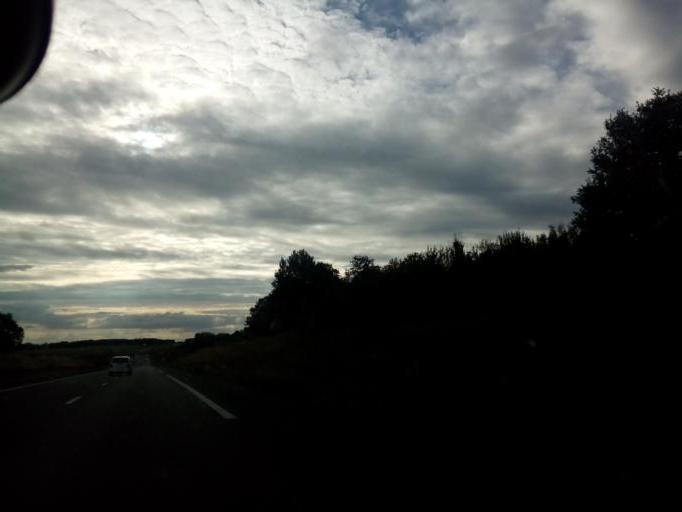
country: FR
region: Centre
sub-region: Departement d'Indre-et-Loire
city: Monts
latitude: 47.3071
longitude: 0.6552
